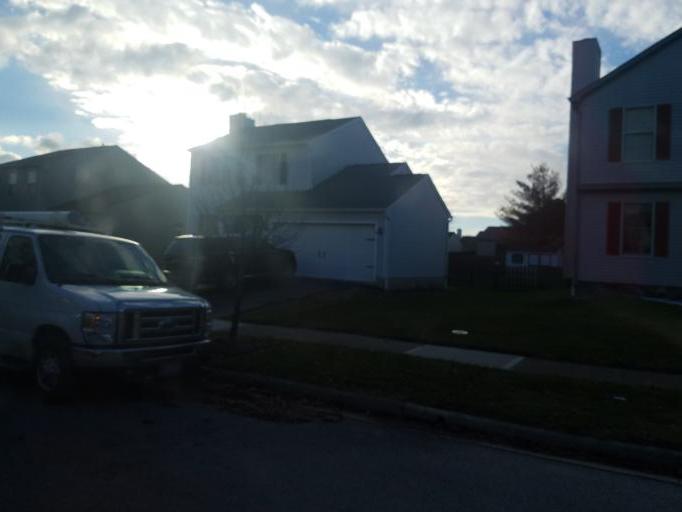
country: US
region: Ohio
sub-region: Delaware County
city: Delaware
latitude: 40.3152
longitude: -83.1060
